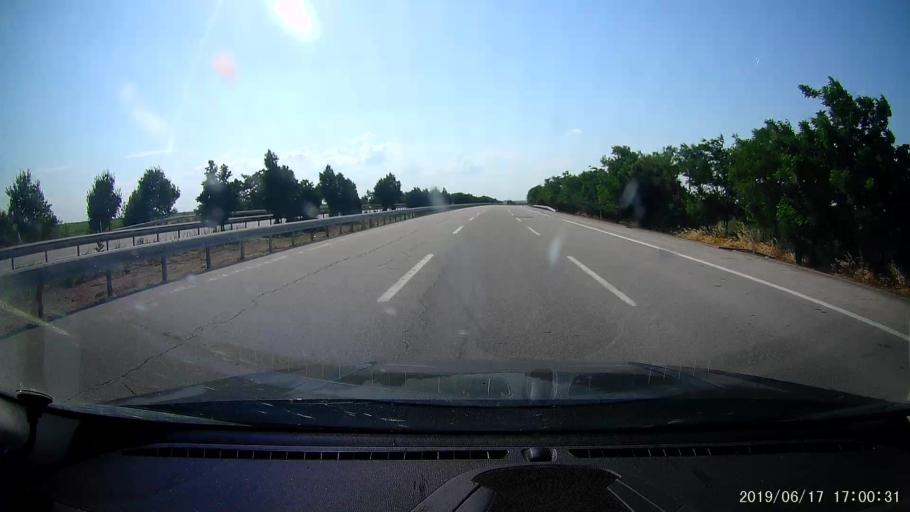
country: TR
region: Edirne
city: Haskoy
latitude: 41.6216
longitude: 26.8294
